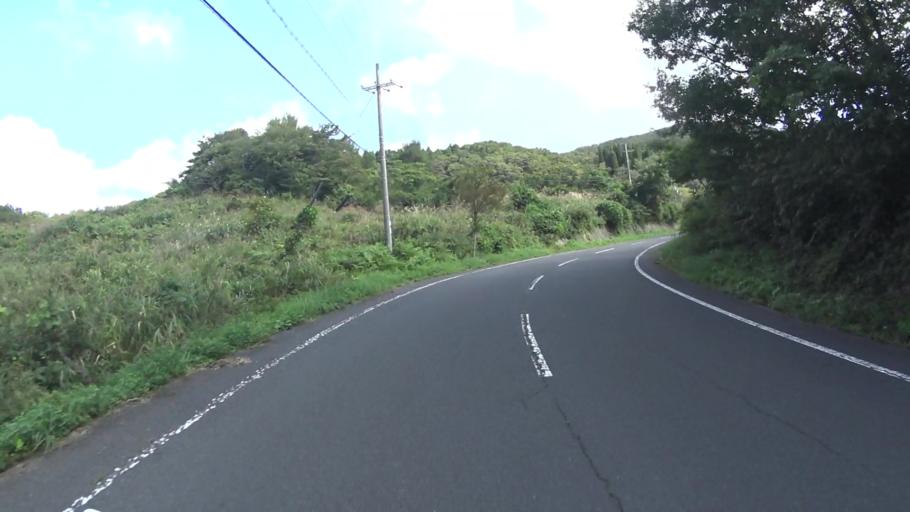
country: JP
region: Kyoto
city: Miyazu
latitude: 35.6433
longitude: 135.1845
